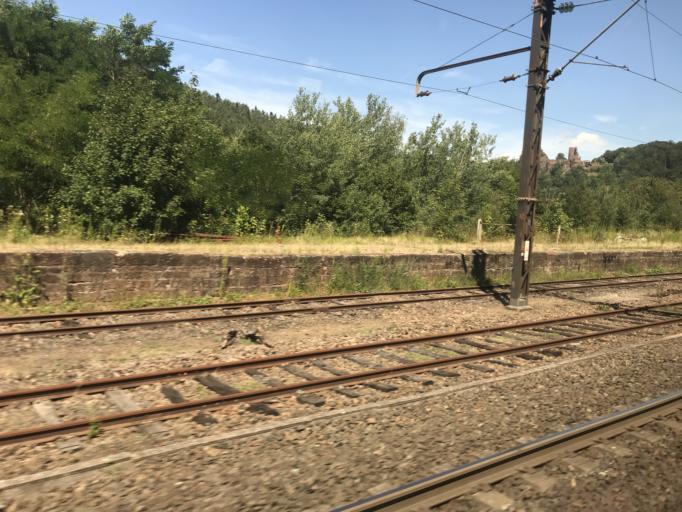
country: FR
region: Lorraine
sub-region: Departement de la Moselle
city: Phalsbourg
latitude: 48.7272
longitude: 7.2445
